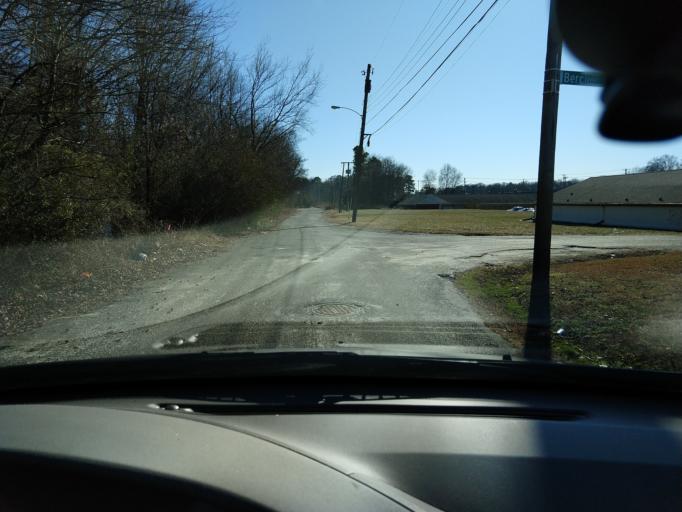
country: US
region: Virginia
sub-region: Chesterfield County
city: Bensley
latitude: 37.4645
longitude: -77.4415
